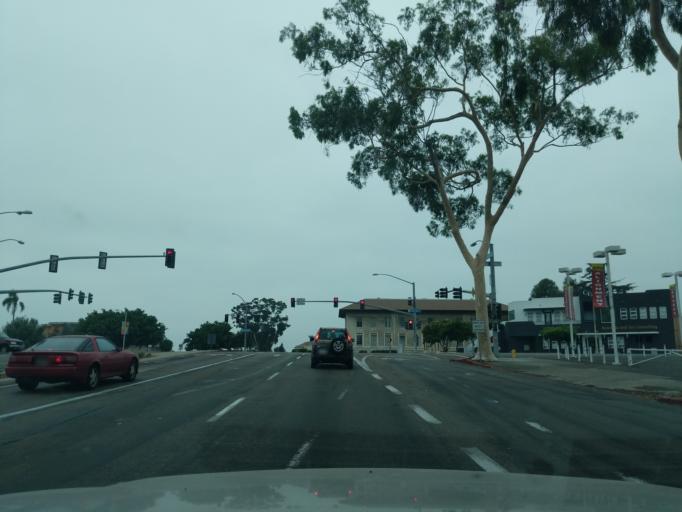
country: US
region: California
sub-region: San Diego County
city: San Diego
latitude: 32.7554
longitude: -117.1457
